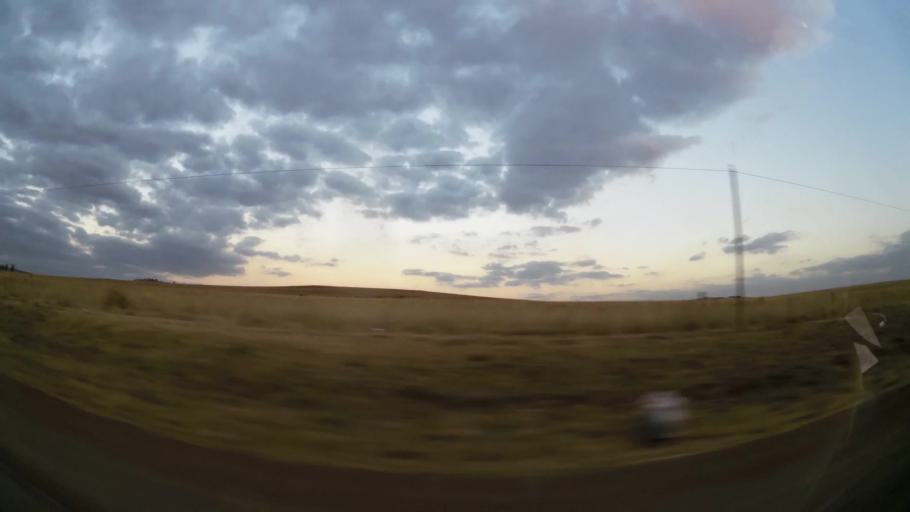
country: ZA
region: Gauteng
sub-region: West Rand District Municipality
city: Krugersdorp
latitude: -26.0514
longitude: 27.7112
